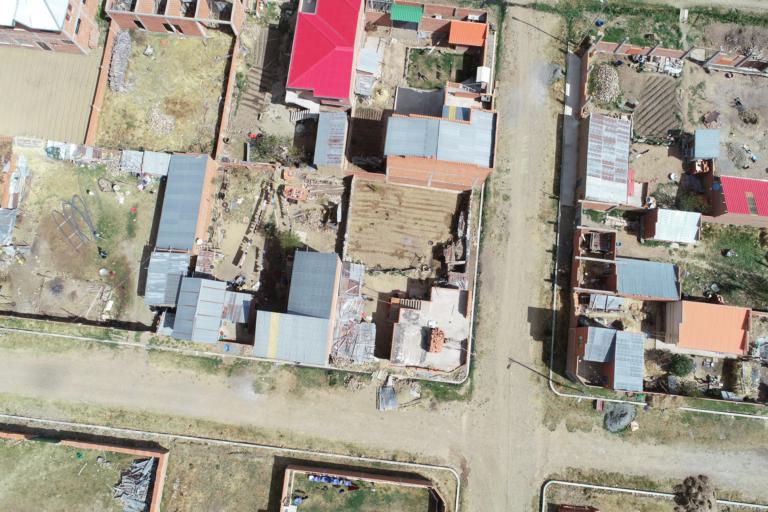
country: BO
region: La Paz
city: Huatajata
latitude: -16.1928
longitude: -68.7458
